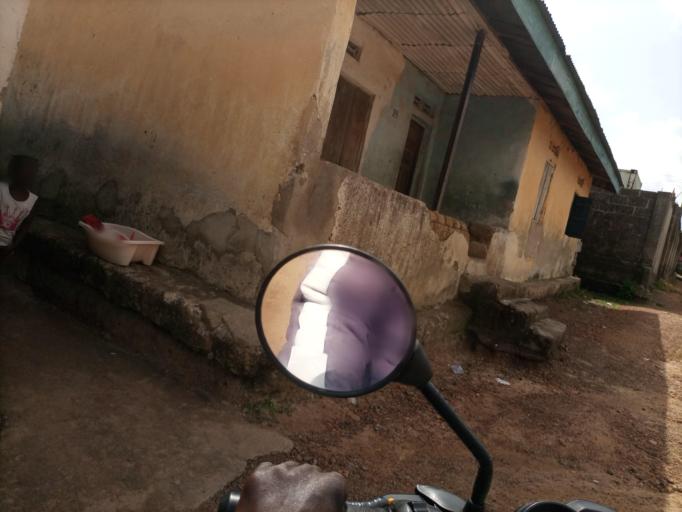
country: SL
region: Southern Province
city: Bo
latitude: 7.9492
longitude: -11.7370
